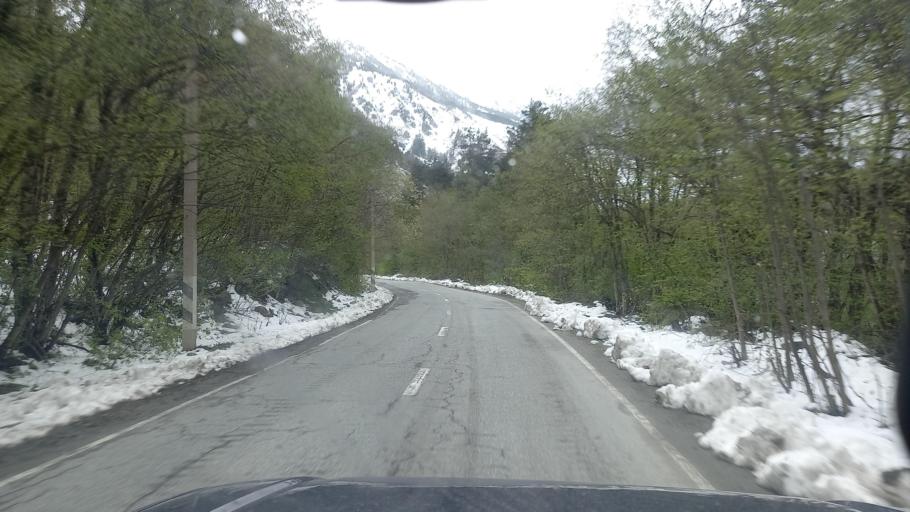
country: RU
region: North Ossetia
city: Mizur
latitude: 42.7941
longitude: 43.9242
